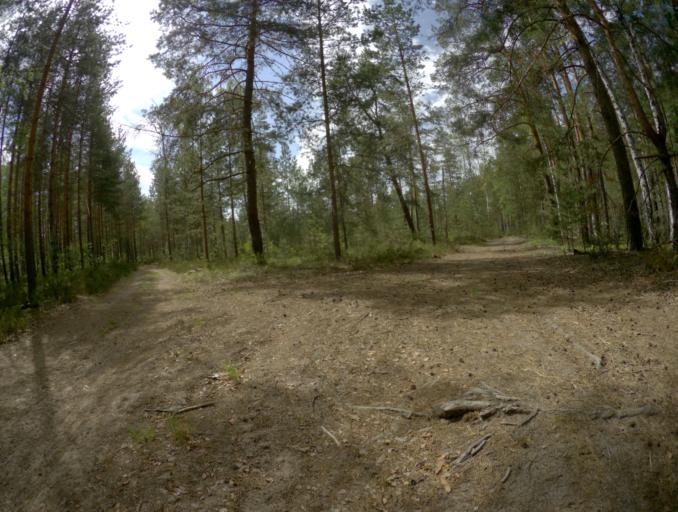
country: RU
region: Vladimir
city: Ivanishchi
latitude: 55.6905
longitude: 40.4130
